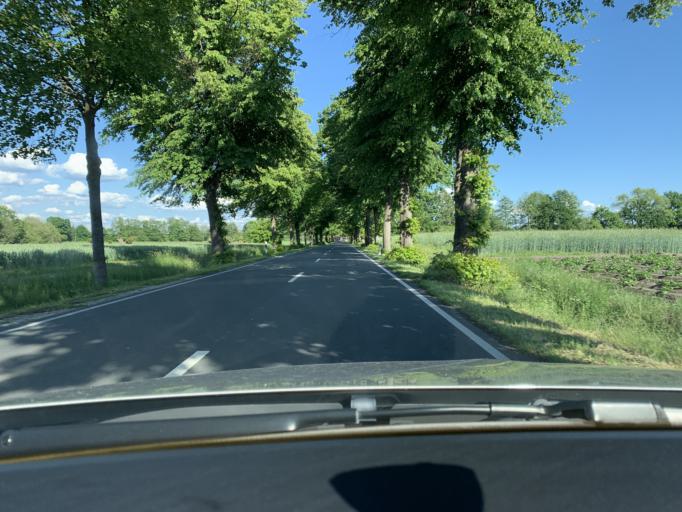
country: DE
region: North Rhine-Westphalia
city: Rietberg
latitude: 51.8173
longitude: 8.4053
